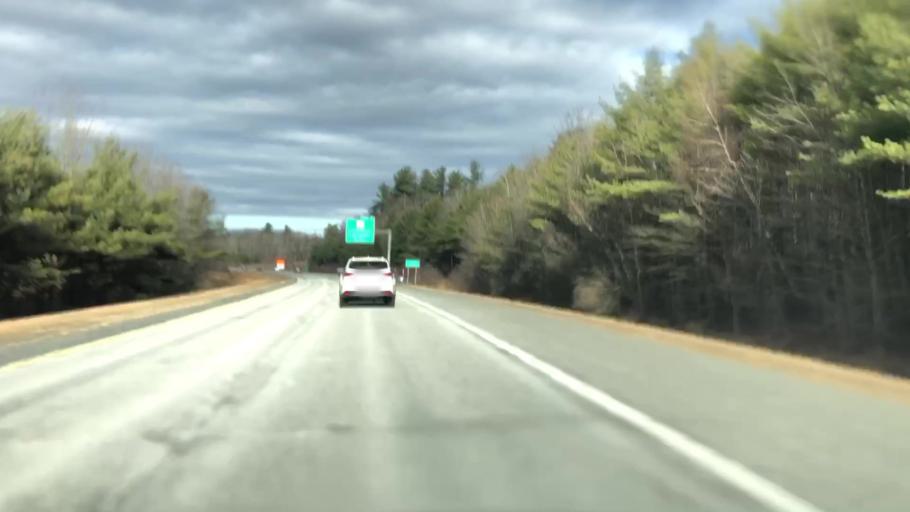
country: US
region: Massachusetts
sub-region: Worcester County
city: South Lancaster
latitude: 42.4735
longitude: -71.7241
